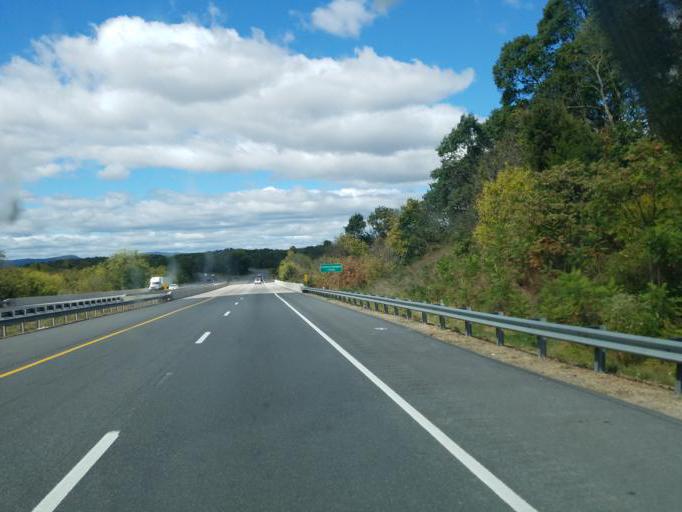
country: US
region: Maryland
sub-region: Washington County
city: Wilson-Conococheague
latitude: 39.6410
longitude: -77.8283
